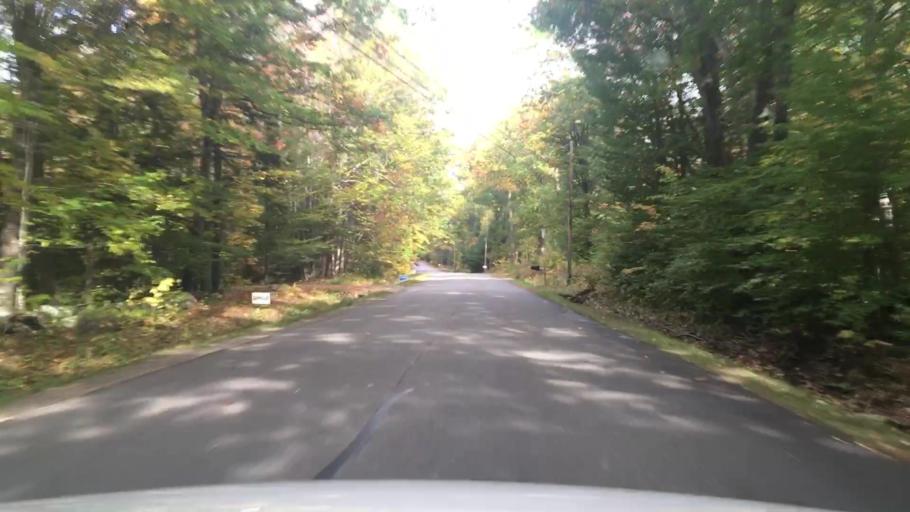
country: US
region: Maine
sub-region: Knox County
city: Camden
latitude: 44.2240
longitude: -69.1030
